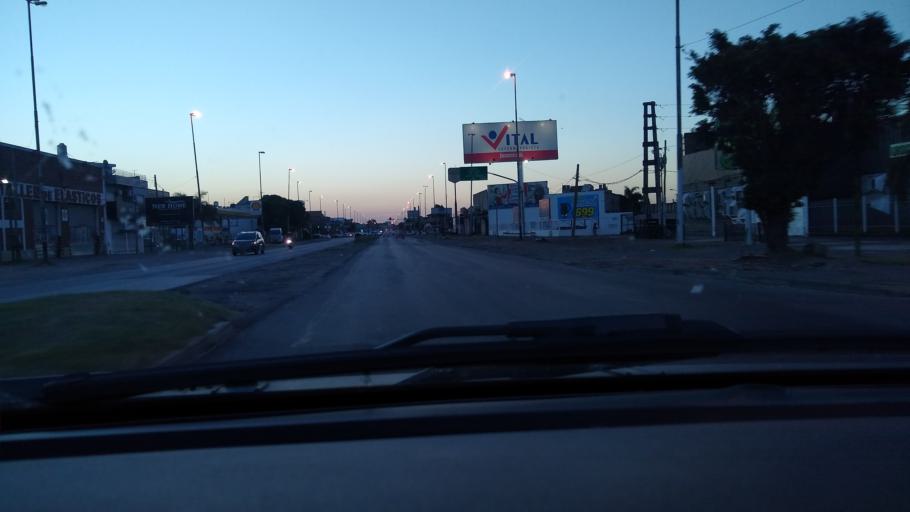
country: AR
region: Buenos Aires
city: San Justo
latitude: -34.6832
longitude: -58.5690
